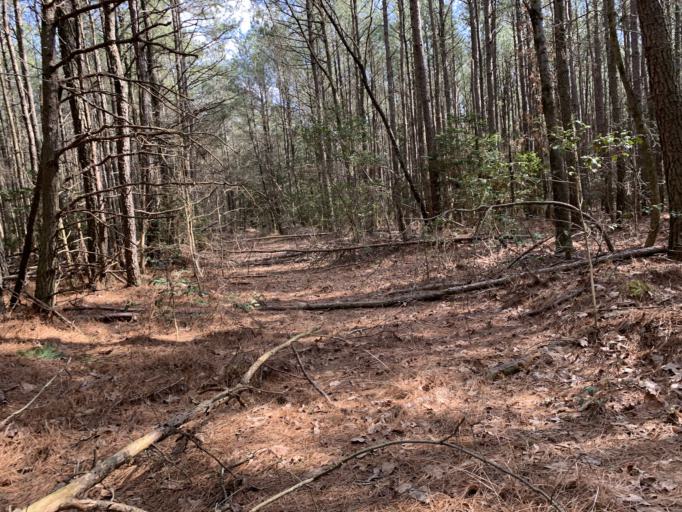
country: US
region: Delaware
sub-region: Sussex County
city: Georgetown
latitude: 38.6783
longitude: -75.4758
